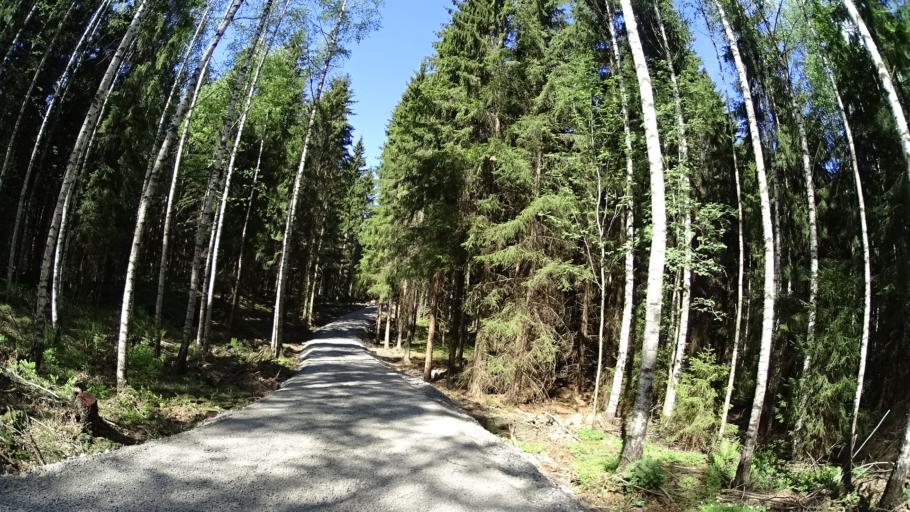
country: FI
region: Uusimaa
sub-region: Helsinki
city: Espoo
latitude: 60.1789
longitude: 24.6263
